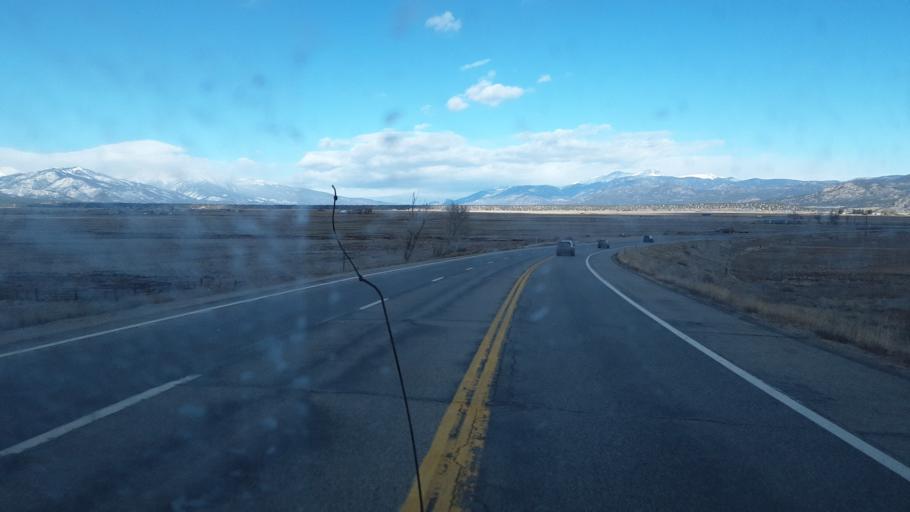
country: US
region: Colorado
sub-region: Chaffee County
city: Buena Vista
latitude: 38.7090
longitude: -106.0913
